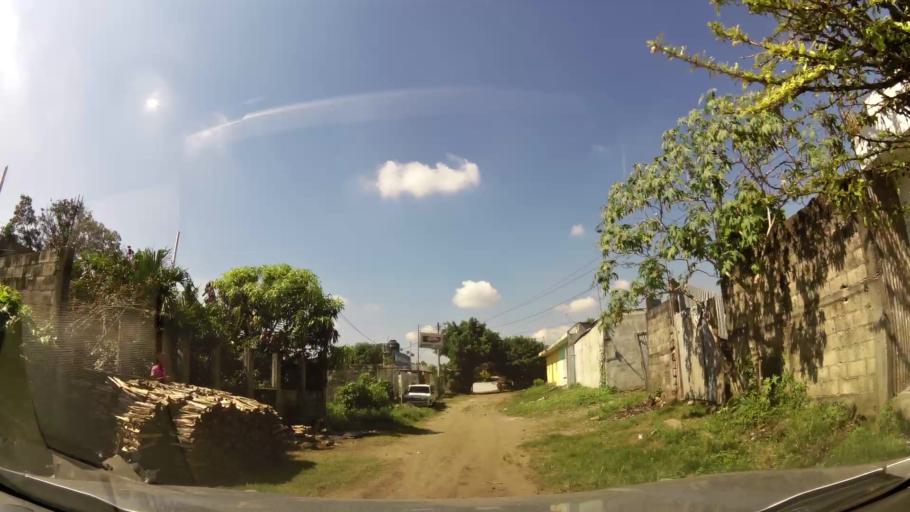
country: GT
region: Suchitepeque
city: Mazatenango
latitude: 14.5311
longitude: -91.4883
